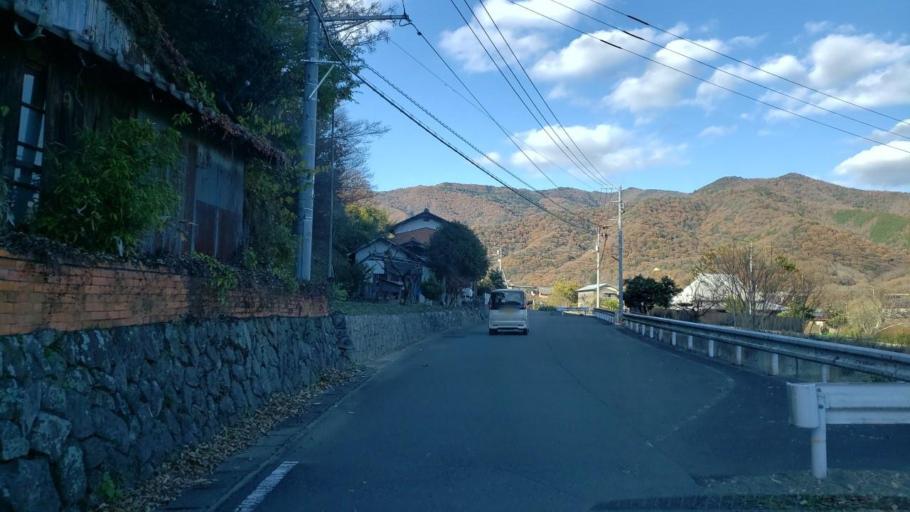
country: JP
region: Tokushima
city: Wakimachi
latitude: 34.0630
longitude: 134.0879
